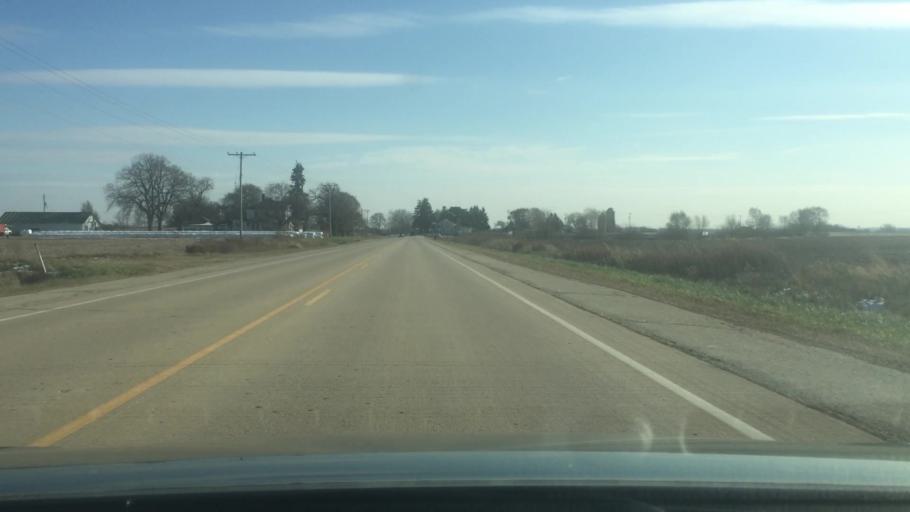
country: US
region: Wisconsin
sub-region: Jefferson County
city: Fort Atkinson
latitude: 42.9528
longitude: -88.8814
